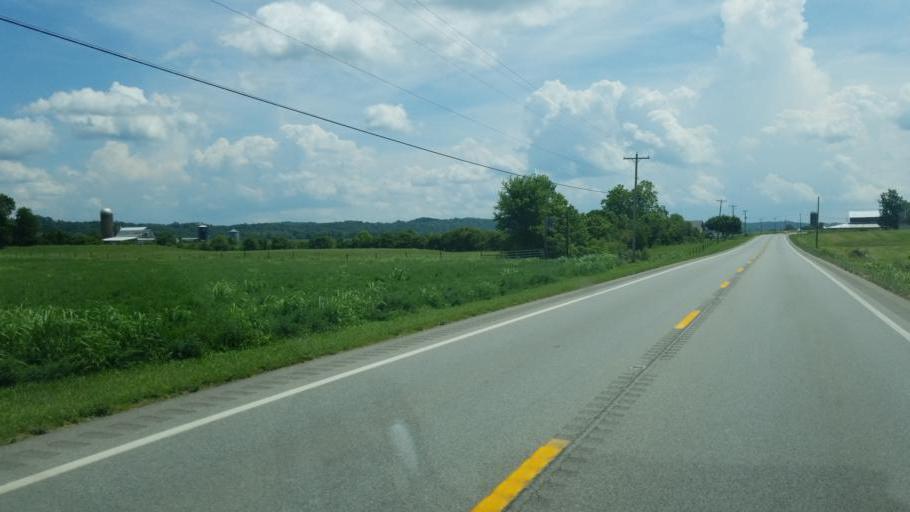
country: US
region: West Virginia
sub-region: Putnam County
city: Buffalo
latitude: 38.7420
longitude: -81.9789
